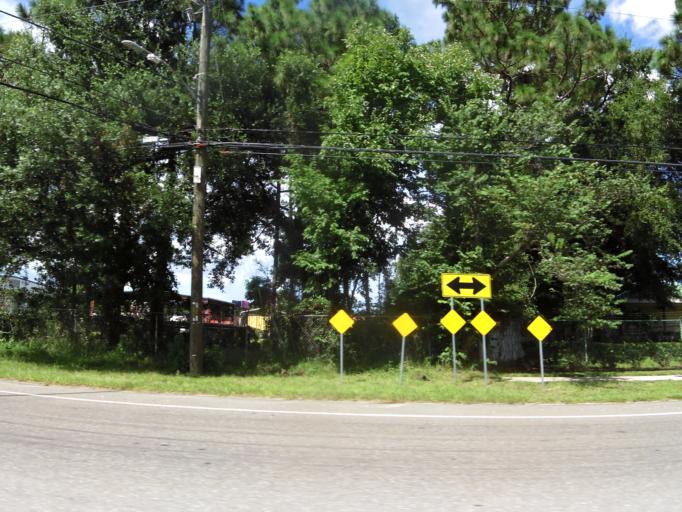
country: US
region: Florida
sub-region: Duval County
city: Jacksonville
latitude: 30.4226
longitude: -81.5728
